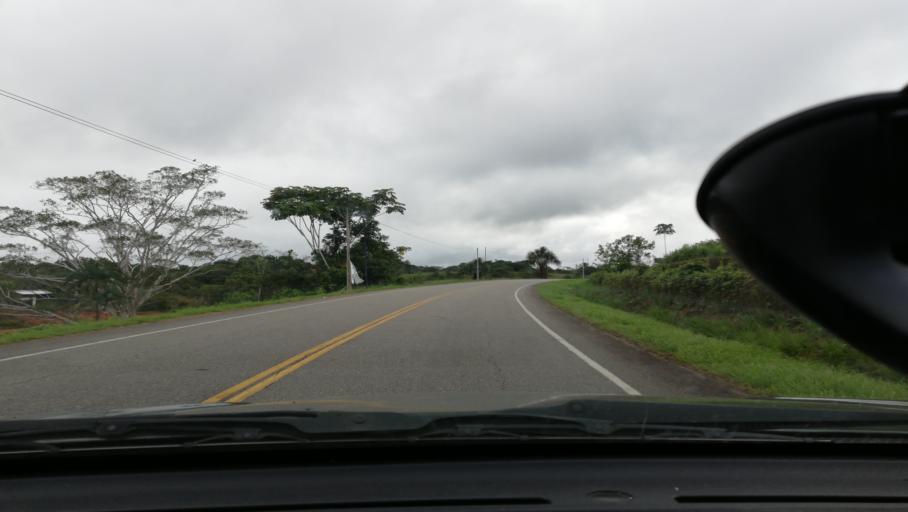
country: PE
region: Loreto
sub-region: Provincia de Loreto
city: Nauta
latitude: -4.4871
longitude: -73.5994
